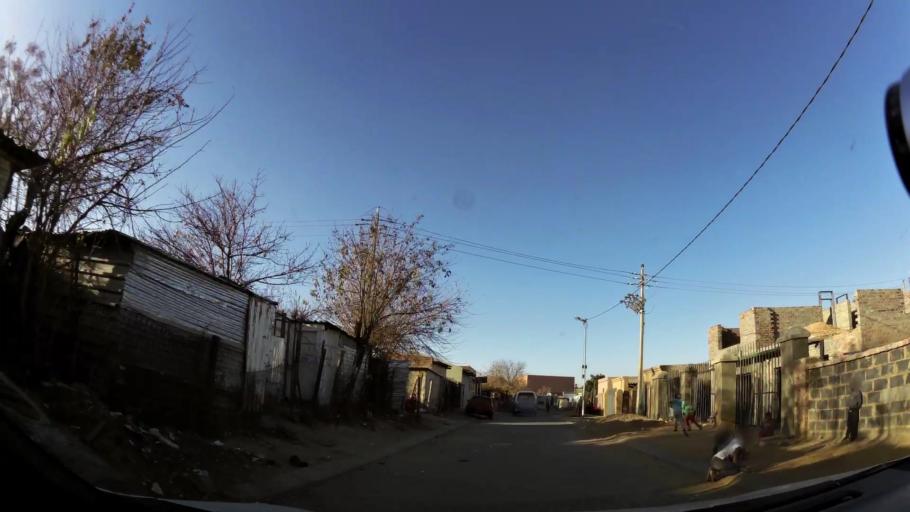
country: ZA
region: Gauteng
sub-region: City of Johannesburg Metropolitan Municipality
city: Diepsloot
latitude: -25.9184
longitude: 28.0222
